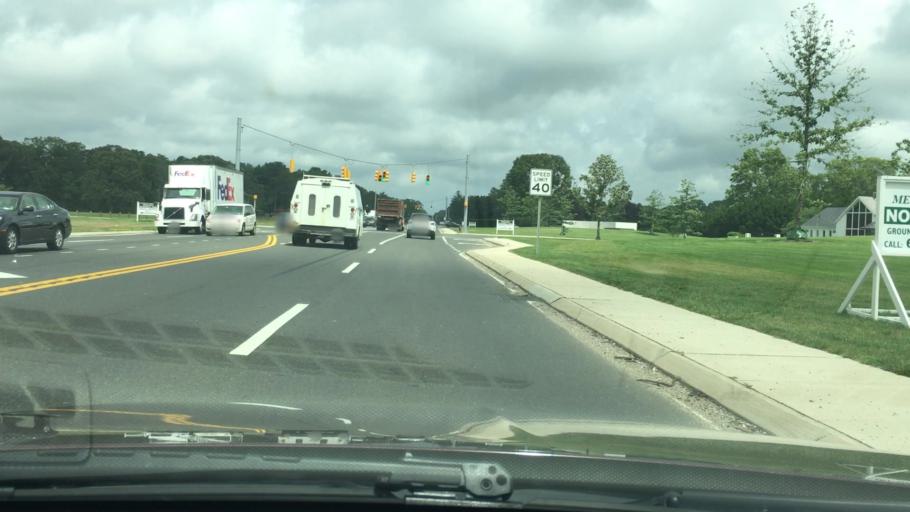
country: US
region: New York
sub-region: Suffolk County
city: East Farmingdale
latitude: 40.7456
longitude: -73.4008
